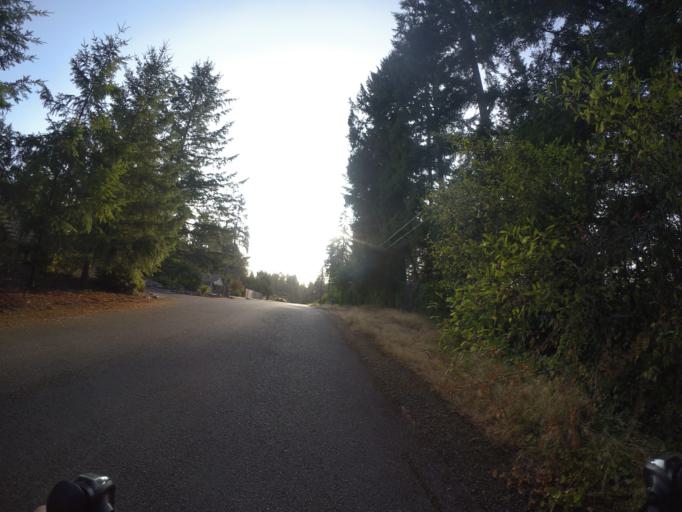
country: US
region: Washington
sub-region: Pierce County
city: Lakewood
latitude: 47.1522
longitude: -122.5180
